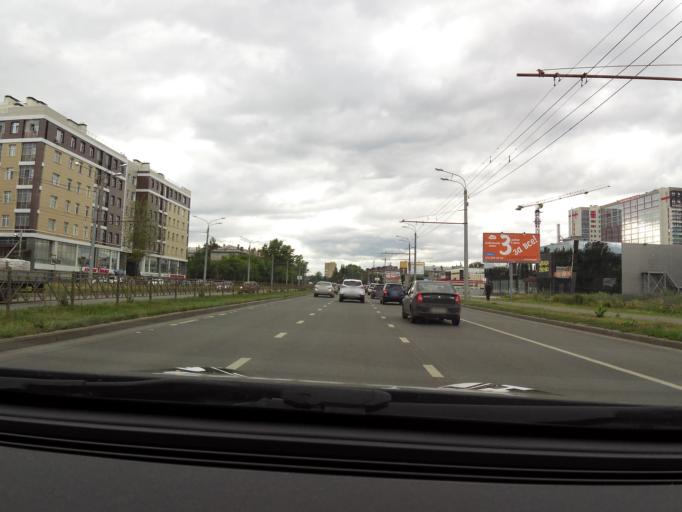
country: RU
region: Tatarstan
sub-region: Gorod Kazan'
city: Kazan
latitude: 55.8159
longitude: 49.0674
